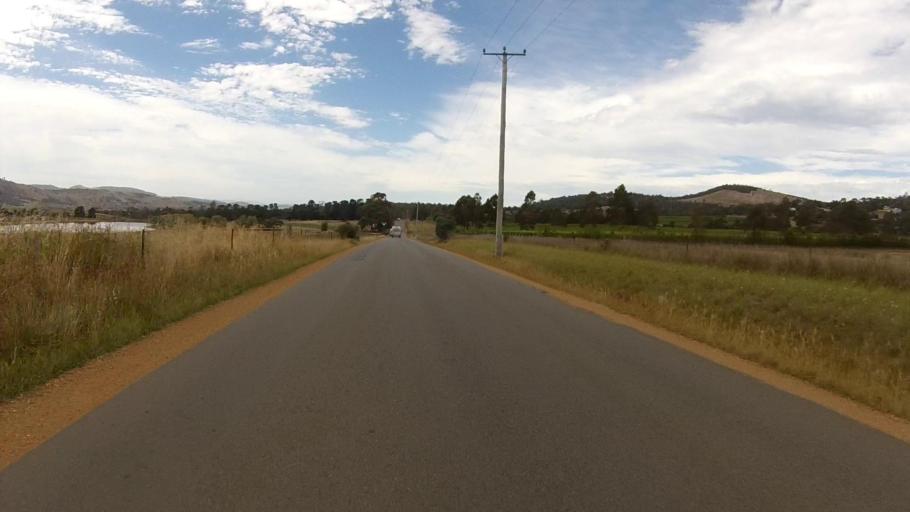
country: AU
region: Tasmania
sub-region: Clarence
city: Lindisfarne
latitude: -42.7579
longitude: 147.3829
